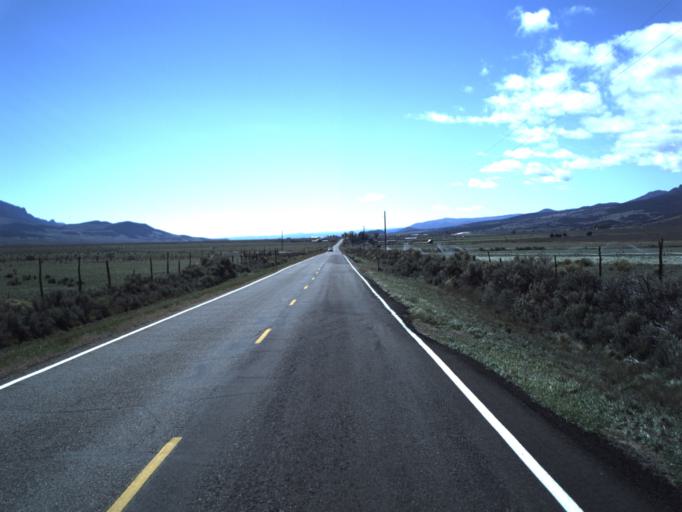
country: US
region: Utah
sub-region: Sevier County
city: Monroe
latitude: 38.4654
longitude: -111.9076
